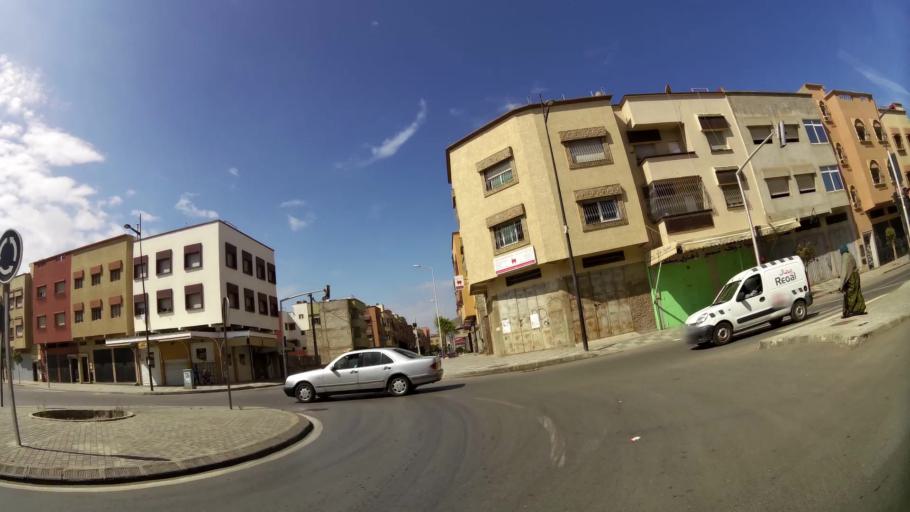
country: MA
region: Rabat-Sale-Zemmour-Zaer
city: Sale
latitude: 34.0721
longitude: -6.7960
